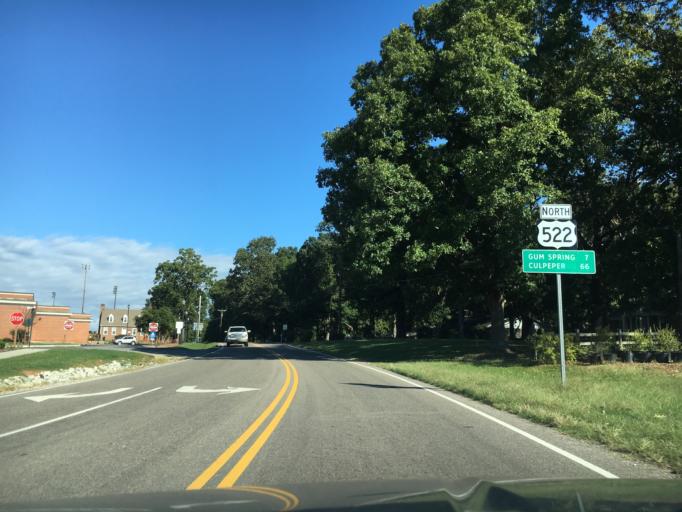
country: US
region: Virginia
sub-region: Goochland County
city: Goochland
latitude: 37.6938
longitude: -77.8872
